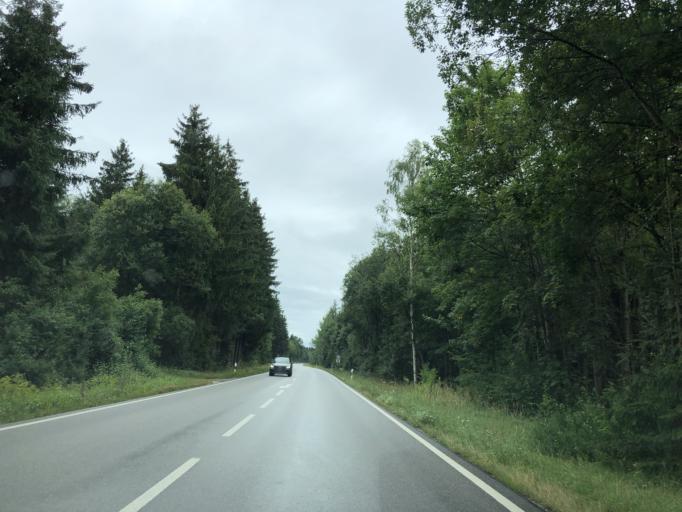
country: DE
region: Bavaria
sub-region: Upper Bavaria
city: Taufkirchen
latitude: 48.0215
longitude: 11.6357
